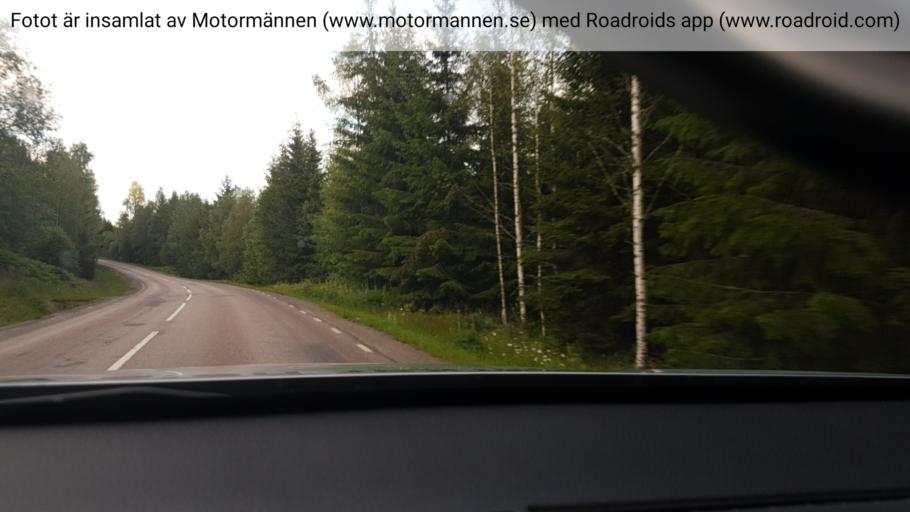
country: SE
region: Vaermland
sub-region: Sunne Kommun
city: Sunne
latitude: 59.9161
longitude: 13.1799
